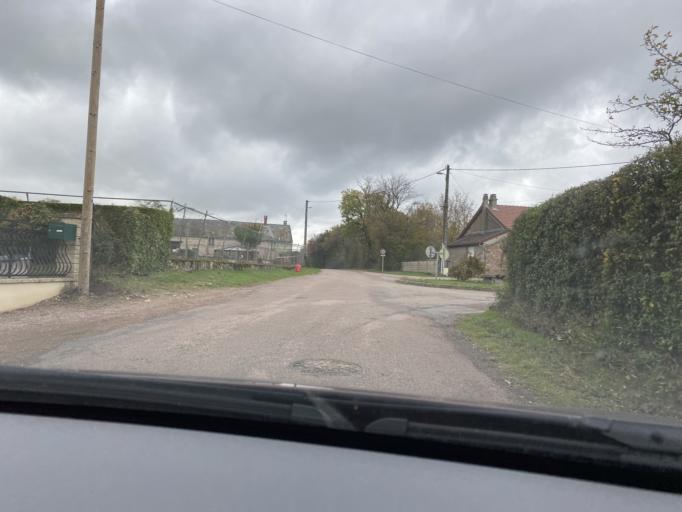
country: FR
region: Bourgogne
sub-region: Departement de la Cote-d'Or
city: Saulieu
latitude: 47.2814
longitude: 4.2184
